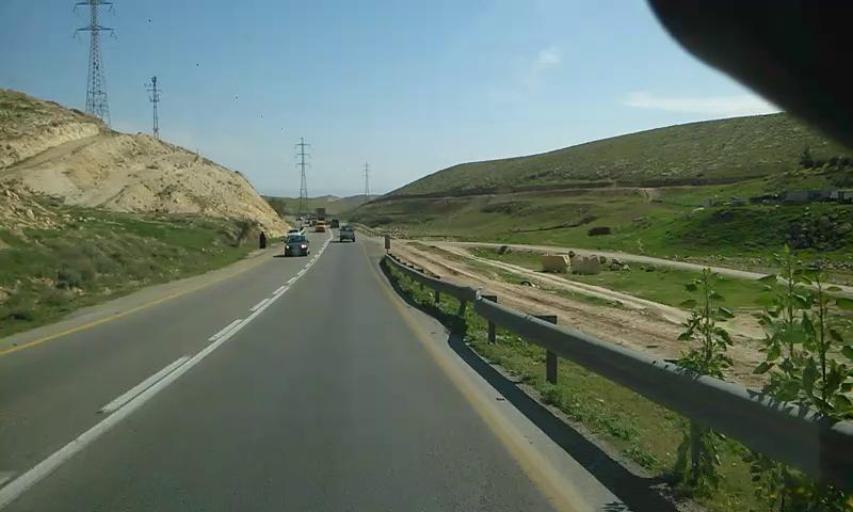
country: PS
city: Az Za`ayyim
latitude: 31.8063
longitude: 35.3116
